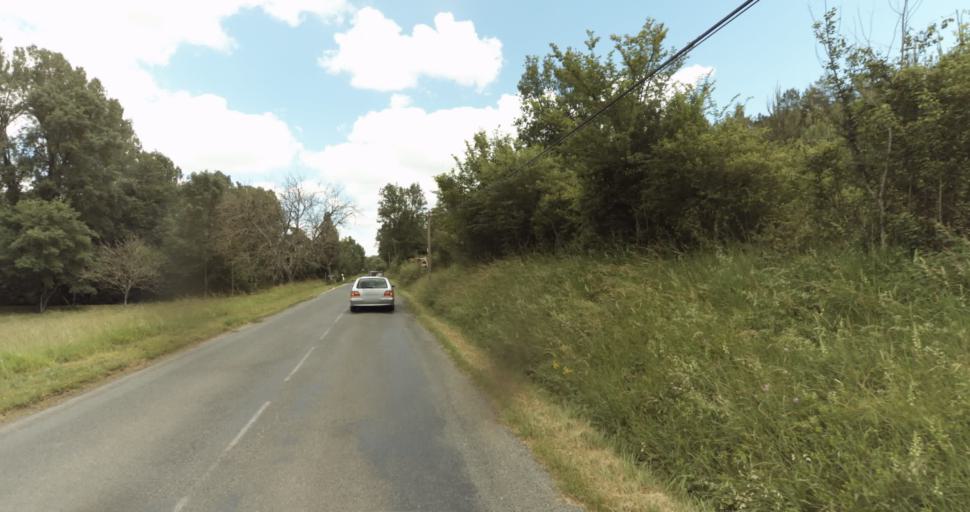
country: FR
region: Aquitaine
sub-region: Departement de la Dordogne
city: Beaumont-du-Perigord
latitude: 44.7563
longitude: 0.7613
